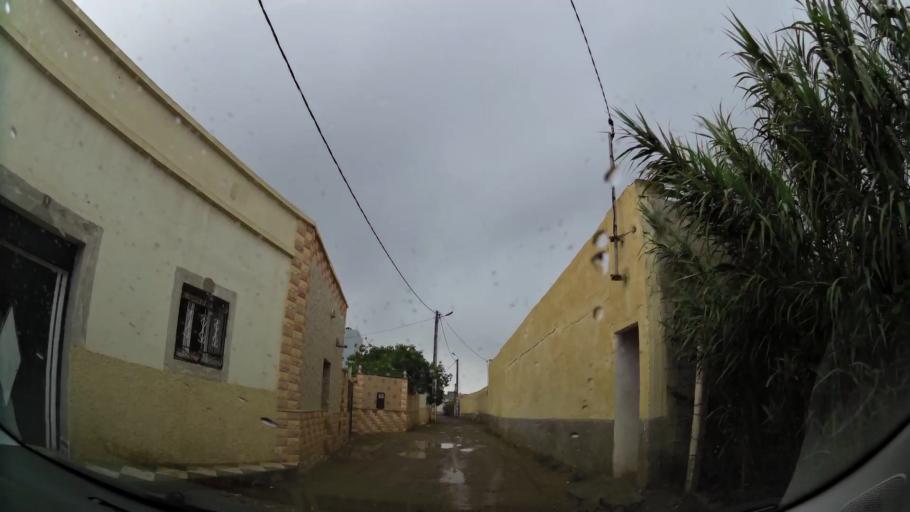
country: MA
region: Oriental
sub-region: Nador
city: Nador
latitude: 35.1561
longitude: -2.9538
